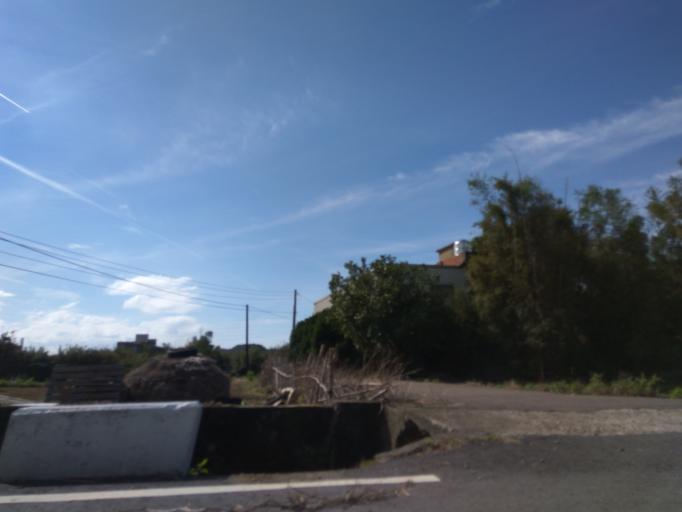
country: TW
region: Taiwan
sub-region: Hsinchu
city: Zhubei
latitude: 24.9942
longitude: 121.0452
